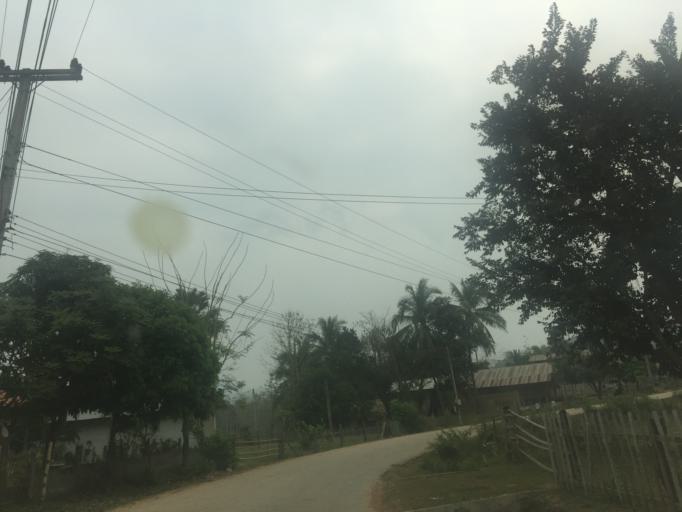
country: LA
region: Vientiane
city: Muang Sanakham
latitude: 18.3881
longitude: 101.5281
